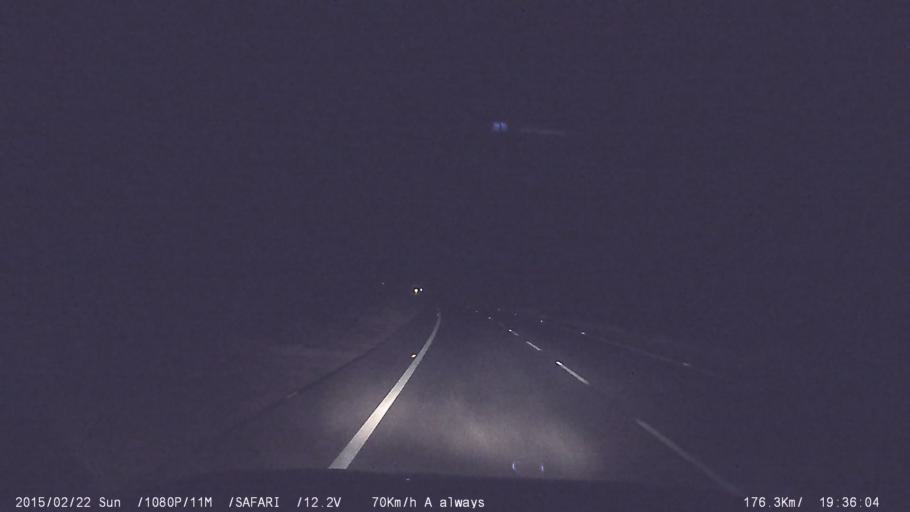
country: IN
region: Tamil Nadu
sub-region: Theni
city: Devadanappatti
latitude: 10.1304
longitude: 77.6107
